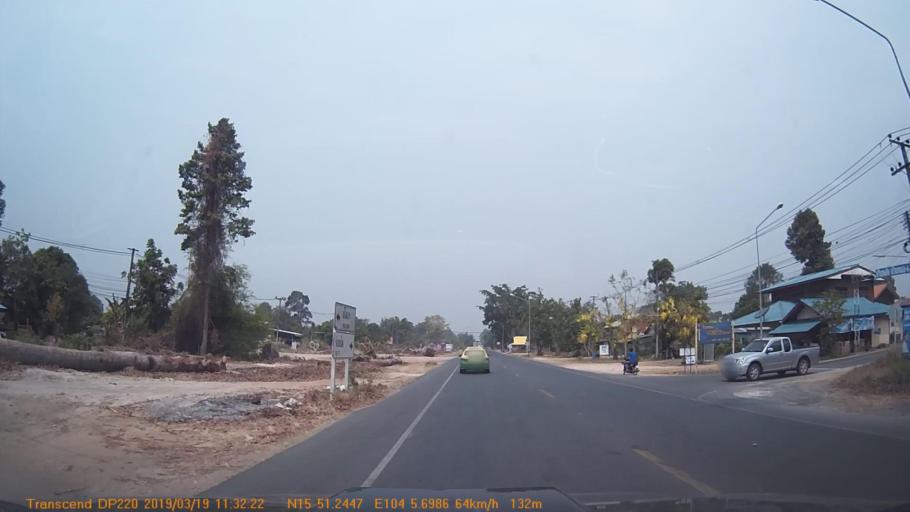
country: TH
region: Yasothon
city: Yasothon
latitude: 15.8543
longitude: 104.0948
